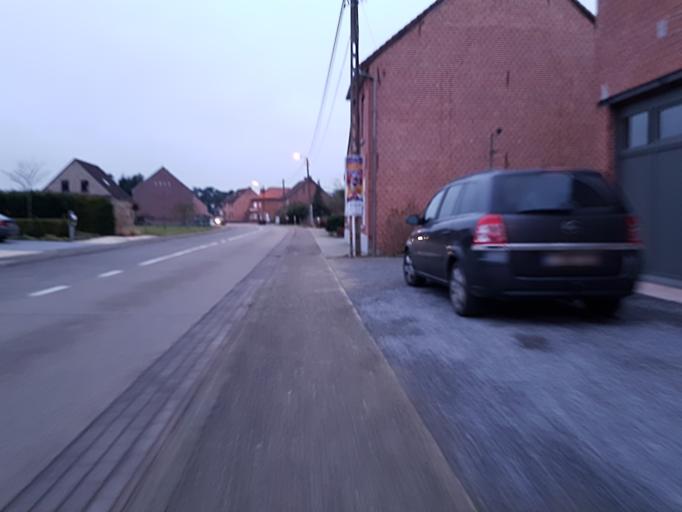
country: BE
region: Flanders
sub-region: Provincie Vlaams-Brabant
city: Rotselaar
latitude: 50.9606
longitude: 4.7058
